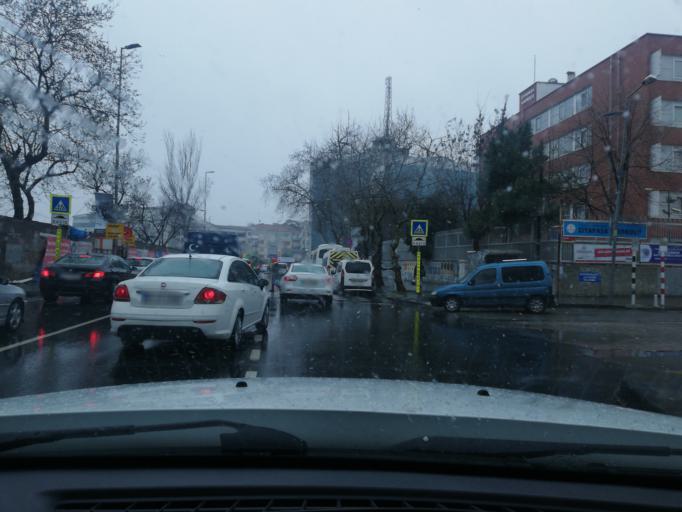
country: TR
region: Istanbul
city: Sisli
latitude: 41.0703
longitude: 28.9811
